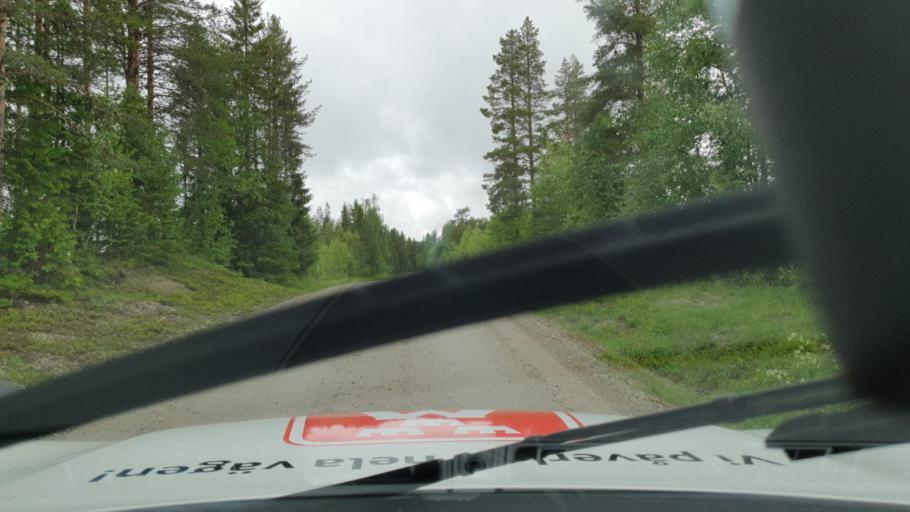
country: SE
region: Vaesterbotten
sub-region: Dorotea Kommun
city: Dorotea
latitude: 64.0330
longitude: 16.7613
